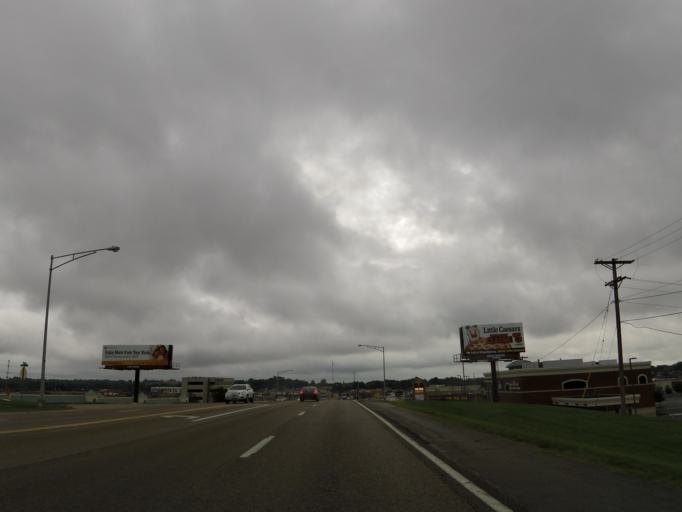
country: US
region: Missouri
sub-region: Cape Girardeau County
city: Cape Girardeau
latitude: 37.3034
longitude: -89.5594
